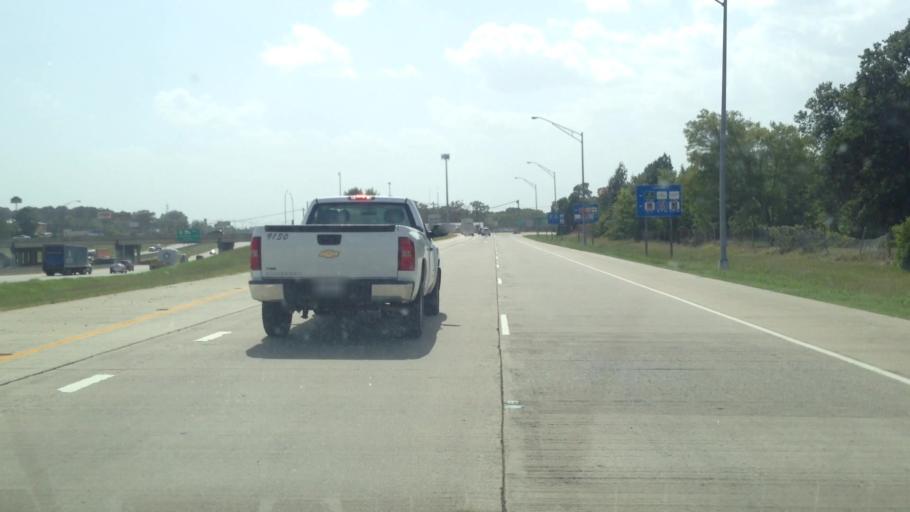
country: US
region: Louisiana
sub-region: Caddo Parish
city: Greenwood
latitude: 32.4513
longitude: -93.8628
